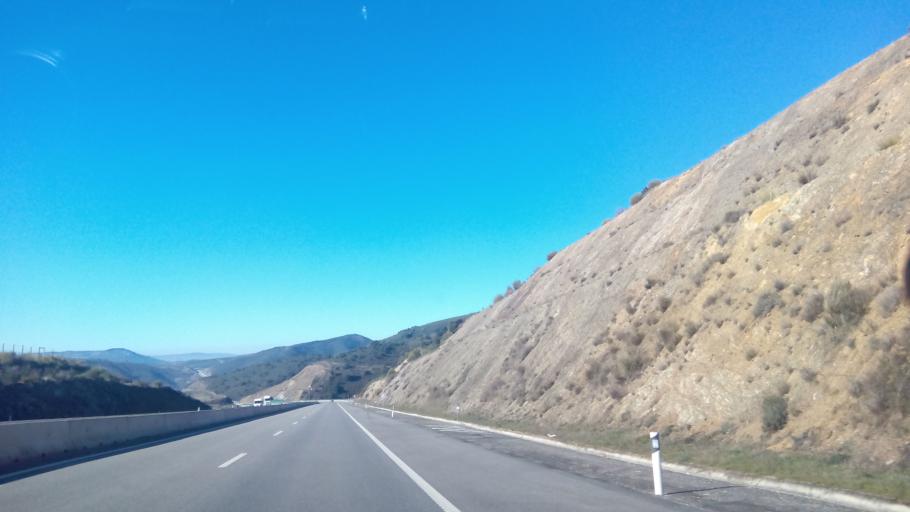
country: PT
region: Braganca
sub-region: Braganca Municipality
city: Braganca
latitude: 41.7659
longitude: -6.6554
